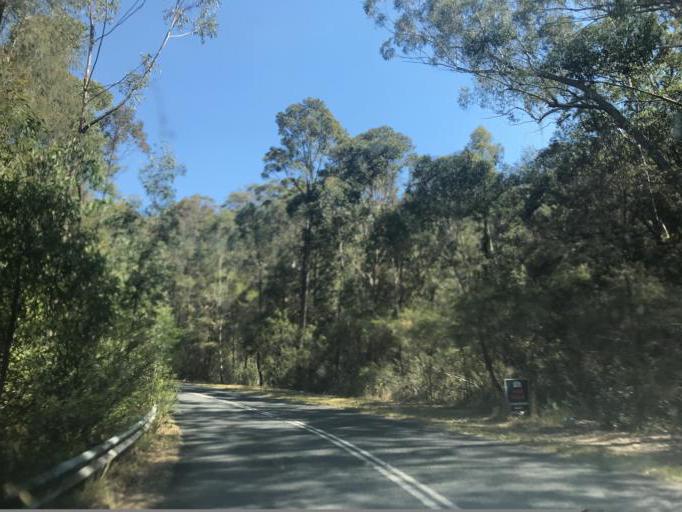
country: AU
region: New South Wales
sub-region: Hawkesbury
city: Pitt Town
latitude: -33.4445
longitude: 150.8796
